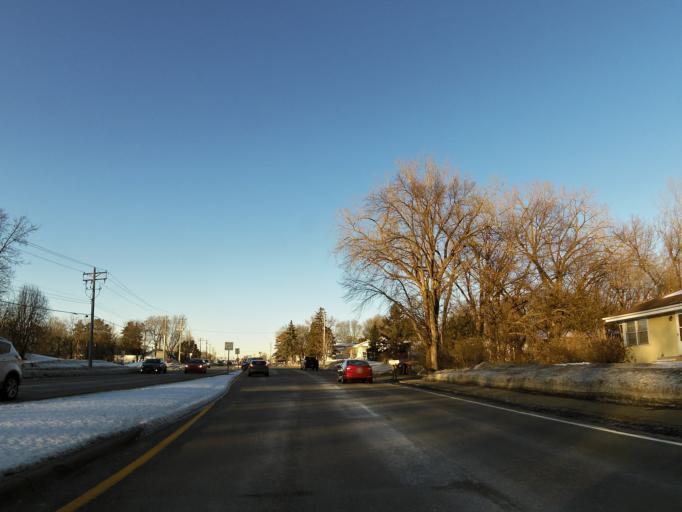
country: US
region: Minnesota
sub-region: Ramsey County
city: North Saint Paul
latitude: 45.0241
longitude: -93.0182
